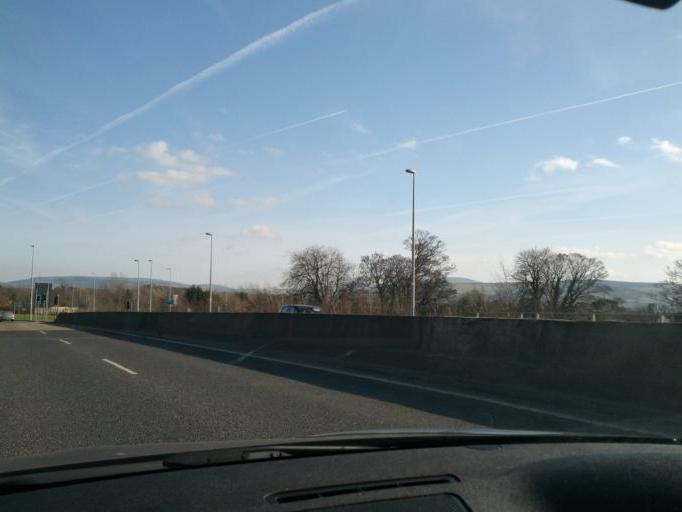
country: IE
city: Jobstown
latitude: 53.3026
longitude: -6.4177
